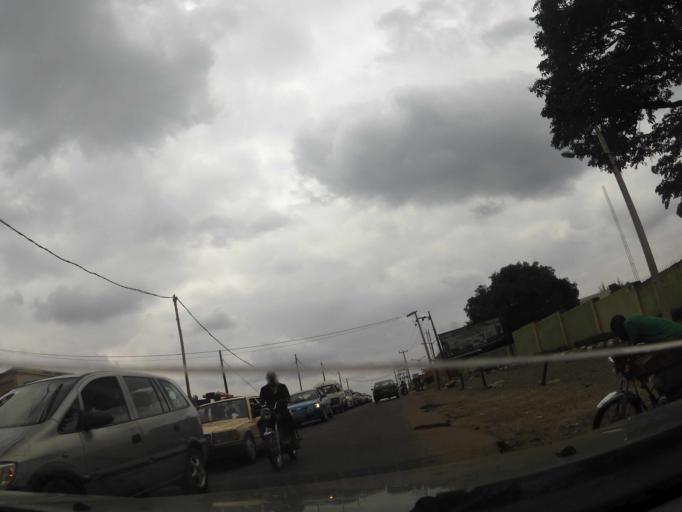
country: NG
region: Oyo
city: Ibadan
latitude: 7.4032
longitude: 3.9254
